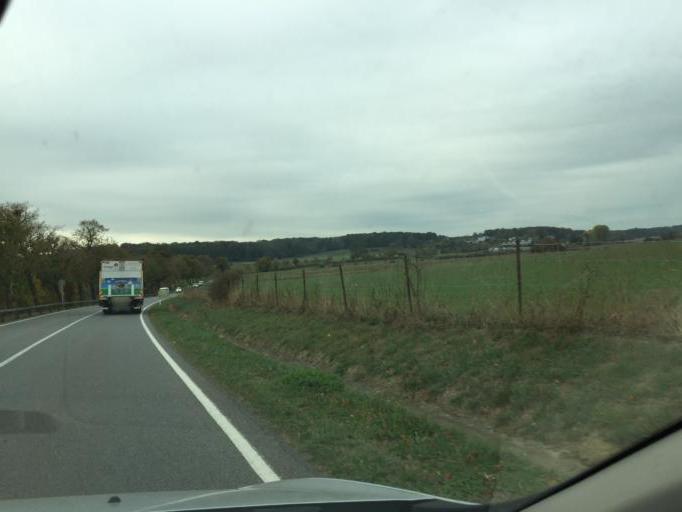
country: LU
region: Luxembourg
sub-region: Canton de Luxembourg
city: Olm
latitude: 49.6634
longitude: 6.0119
